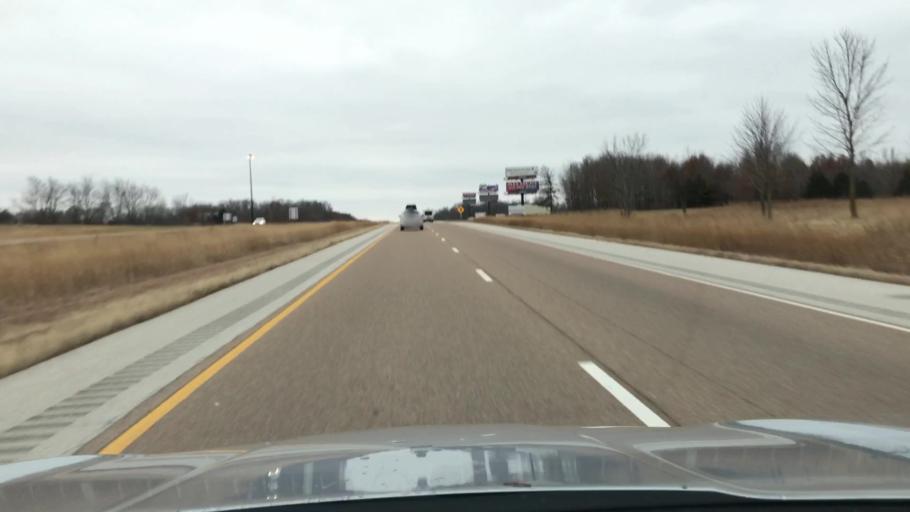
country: US
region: Illinois
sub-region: Macoupin County
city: Mount Olive
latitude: 39.0709
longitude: -89.7559
